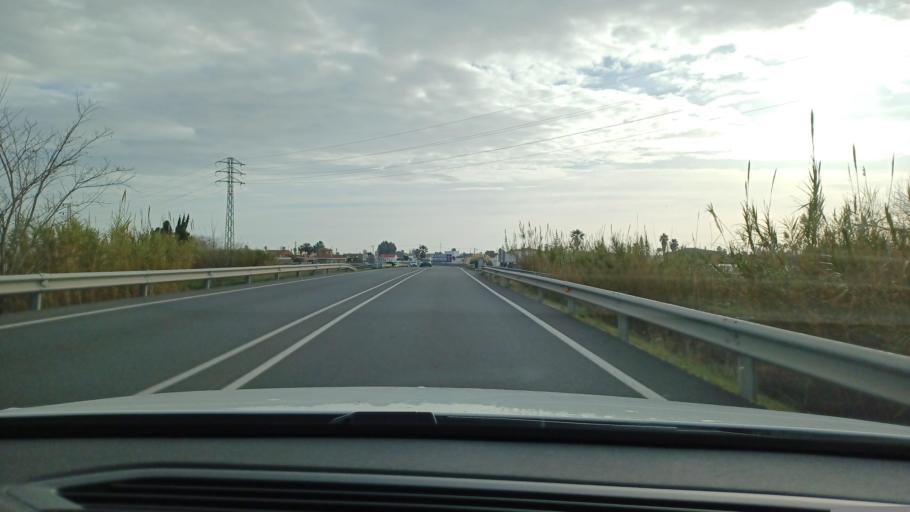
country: ES
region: Catalonia
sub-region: Provincia de Tarragona
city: Deltebre
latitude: 40.7296
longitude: 0.6844
